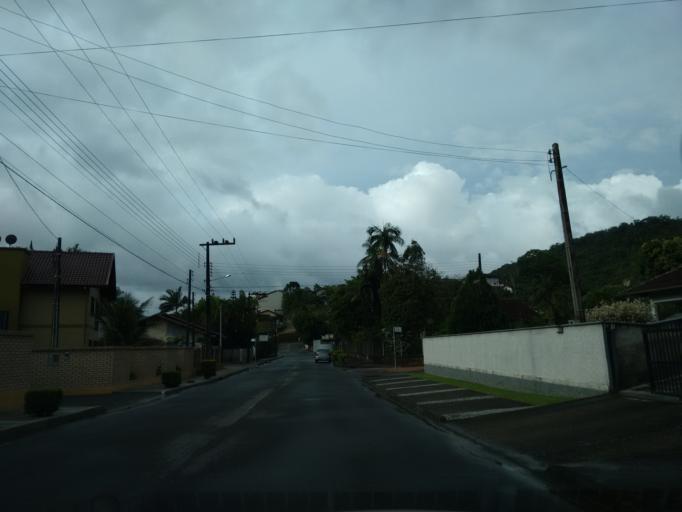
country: BR
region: Santa Catarina
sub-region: Pomerode
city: Pomerode
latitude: -26.7280
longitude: -49.1691
